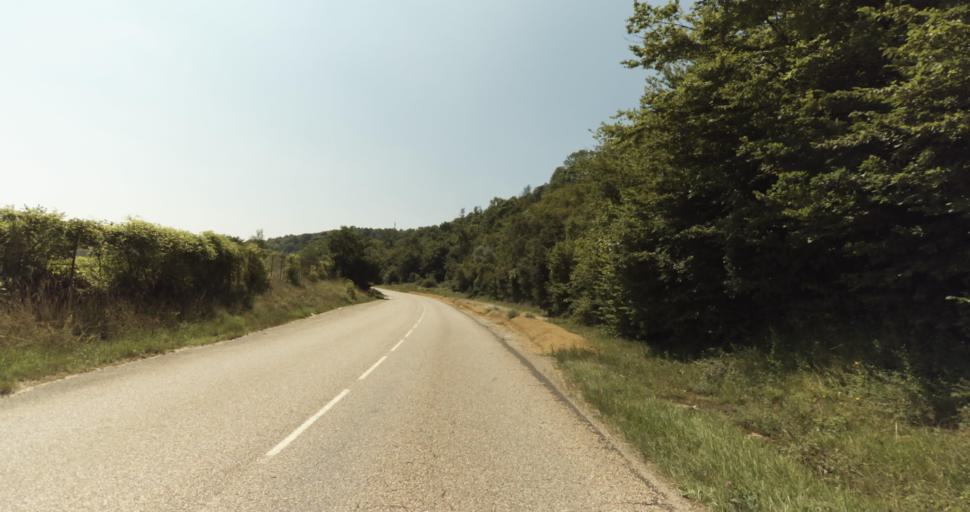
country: FR
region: Lorraine
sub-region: Departement de Meurthe-et-Moselle
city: Joeuf
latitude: 49.2463
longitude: 6.0269
